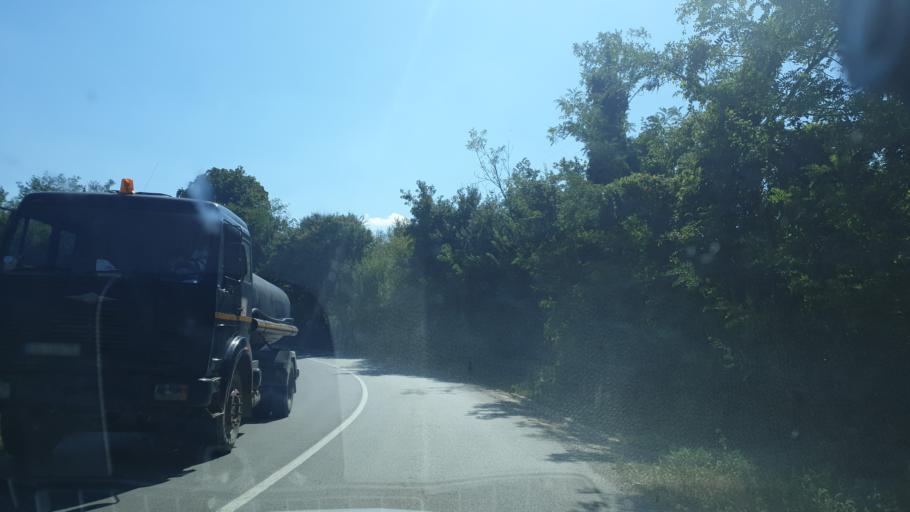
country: RS
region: Central Serbia
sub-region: Kolubarski Okrug
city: Mionica
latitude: 44.1950
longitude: 20.0263
